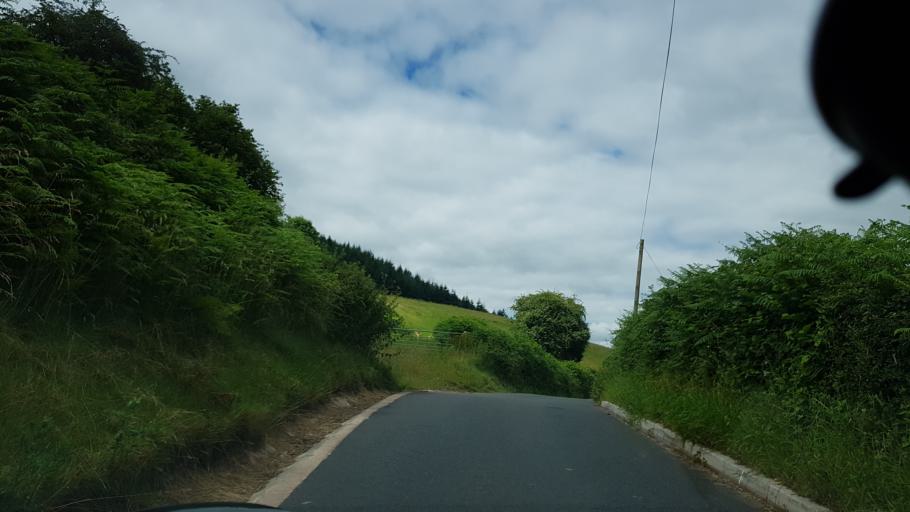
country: GB
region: Wales
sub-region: Monmouthshire
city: Grosmont
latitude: 51.8944
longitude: -2.8287
